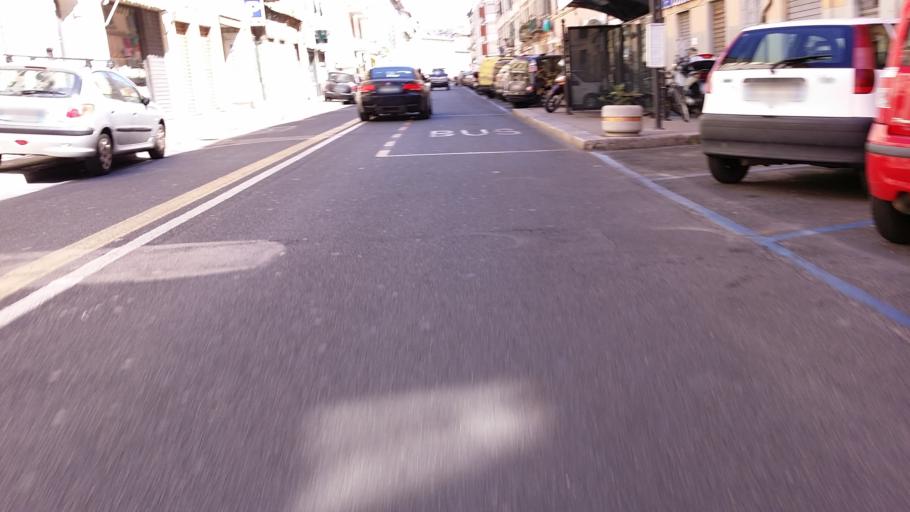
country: IT
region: Tuscany
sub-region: Provincia di Livorno
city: Livorno
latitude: 43.5545
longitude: 10.3151
